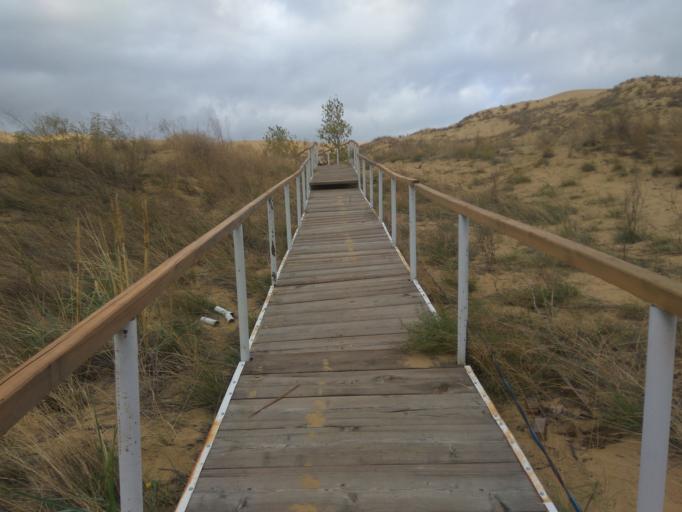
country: RU
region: Dagestan
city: Korkmaskala
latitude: 43.0048
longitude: 47.2364
